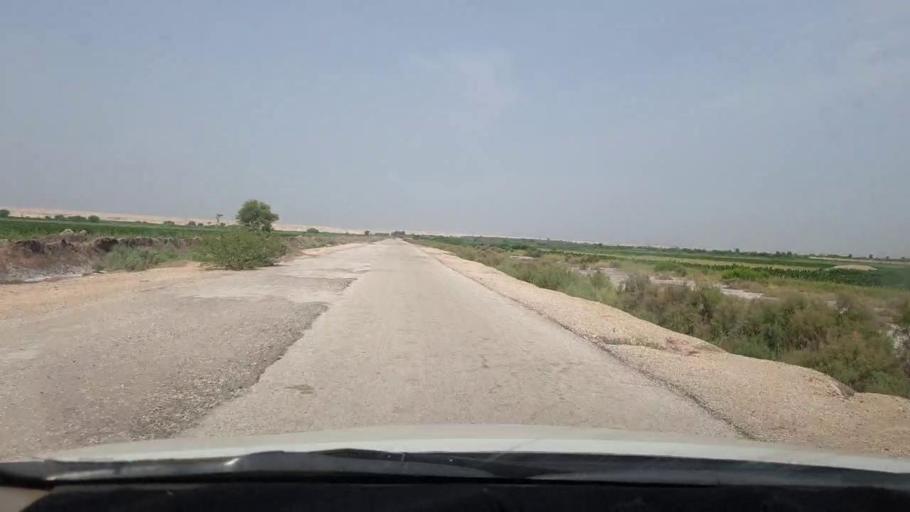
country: PK
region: Sindh
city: Rohri
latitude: 27.5948
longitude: 69.0002
